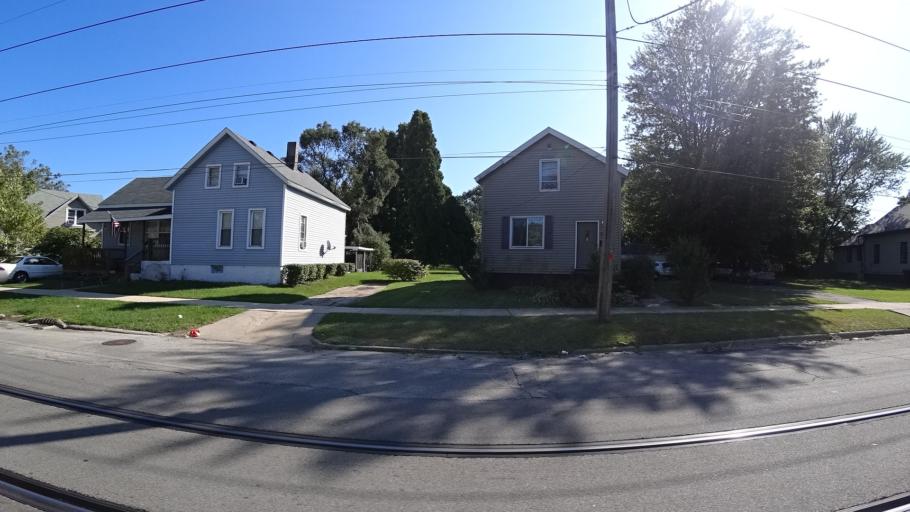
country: US
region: Indiana
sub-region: LaPorte County
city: Michigan City
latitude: 41.7084
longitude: -86.9123
